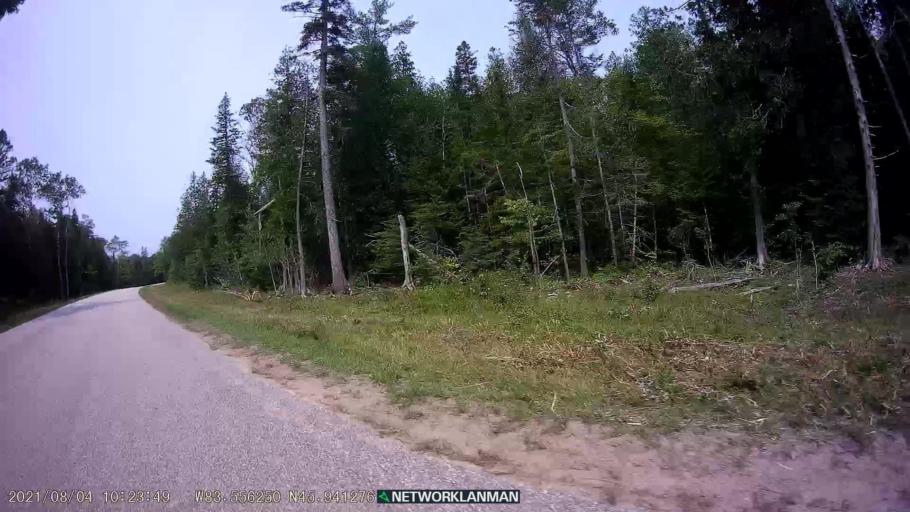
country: CA
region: Ontario
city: Thessalon
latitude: 45.9413
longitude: -83.5566
